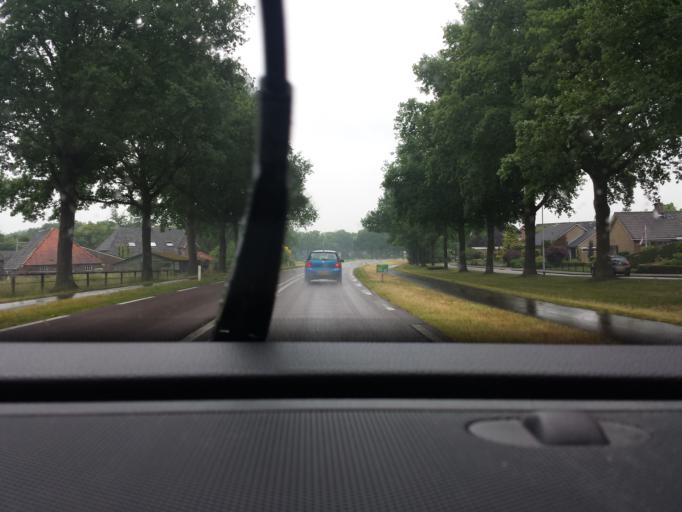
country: NL
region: Gelderland
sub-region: Berkelland
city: Neede
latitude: 52.1397
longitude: 6.6186
